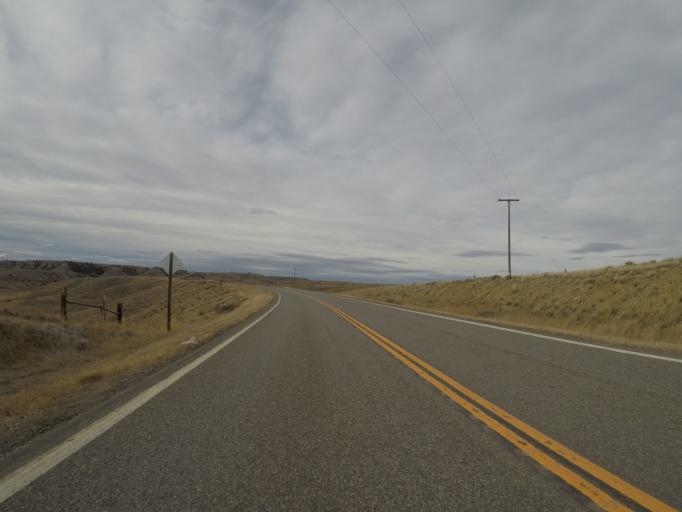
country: US
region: Montana
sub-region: Yellowstone County
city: Laurel
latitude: 45.8471
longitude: -108.7368
